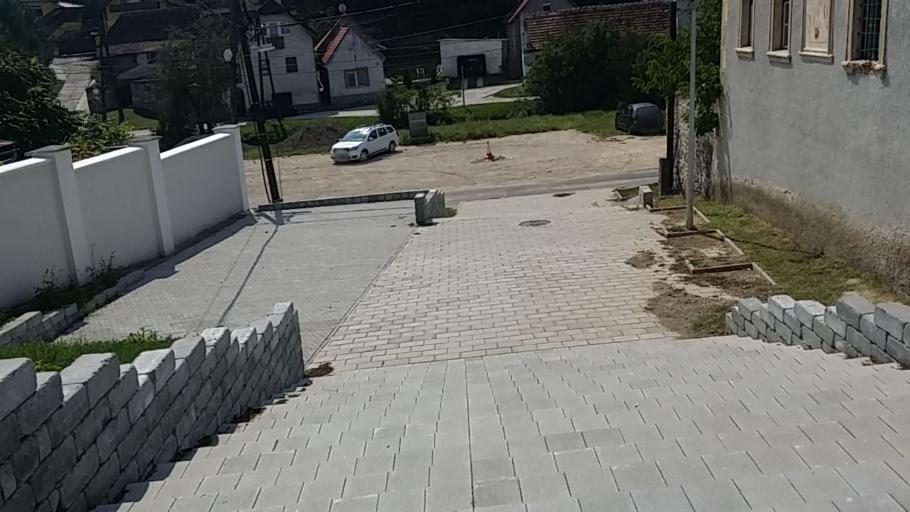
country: HU
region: Gyor-Moson-Sopron
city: Fertorakos
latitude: 47.7174
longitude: 16.6524
